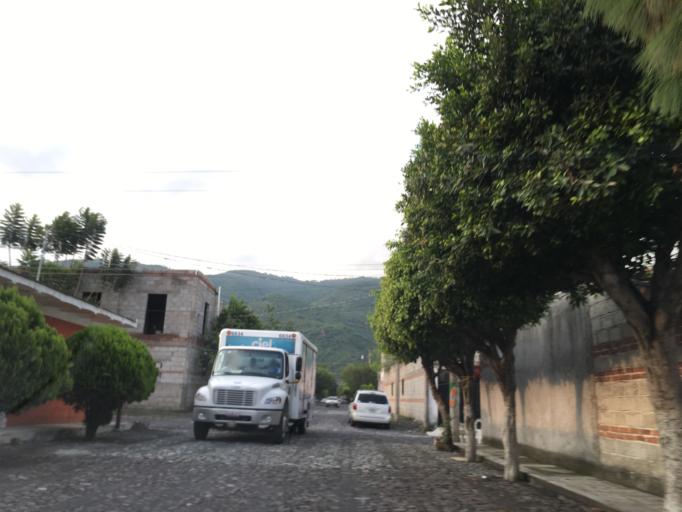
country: MX
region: Nayarit
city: Jala
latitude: 21.0993
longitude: -104.4352
